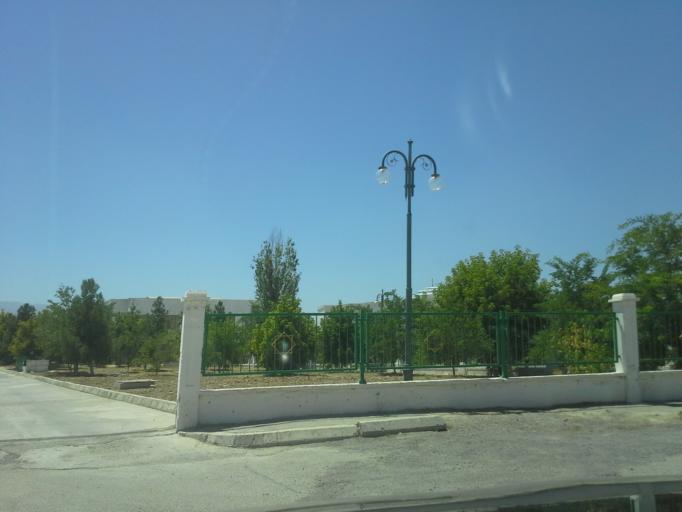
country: TM
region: Ahal
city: Abadan
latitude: 38.0270
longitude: 58.2631
